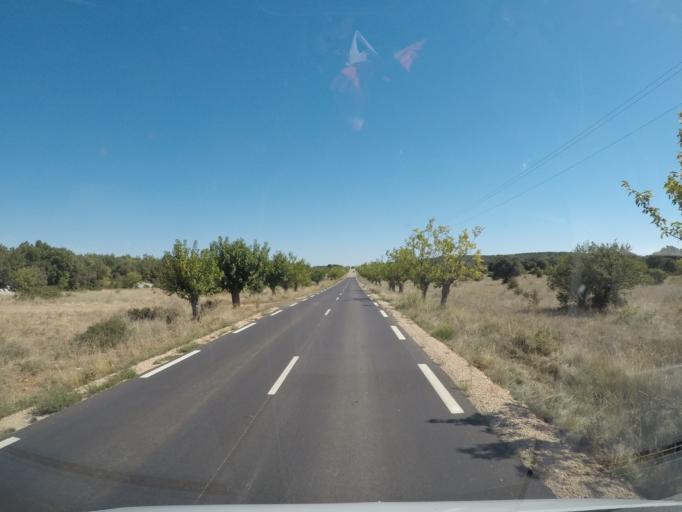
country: FR
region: Languedoc-Roussillon
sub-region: Departement de l'Herault
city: Aniane
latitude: 43.7268
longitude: 3.6570
